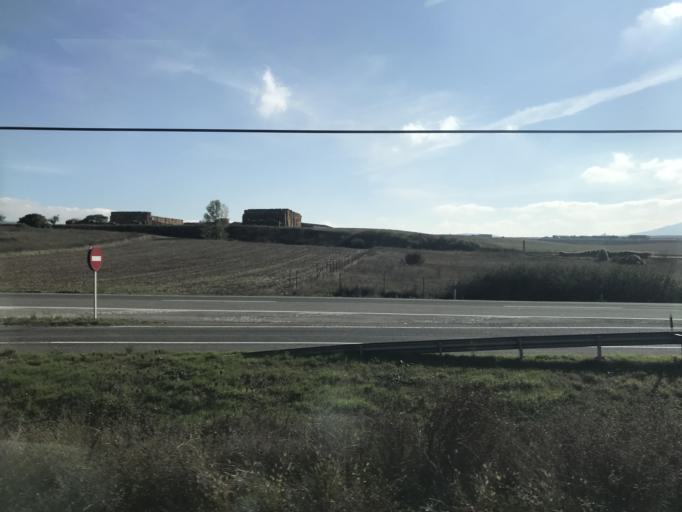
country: ES
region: Basque Country
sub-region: Provincia de Alava
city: Arminon
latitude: 42.7613
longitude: -2.8309
